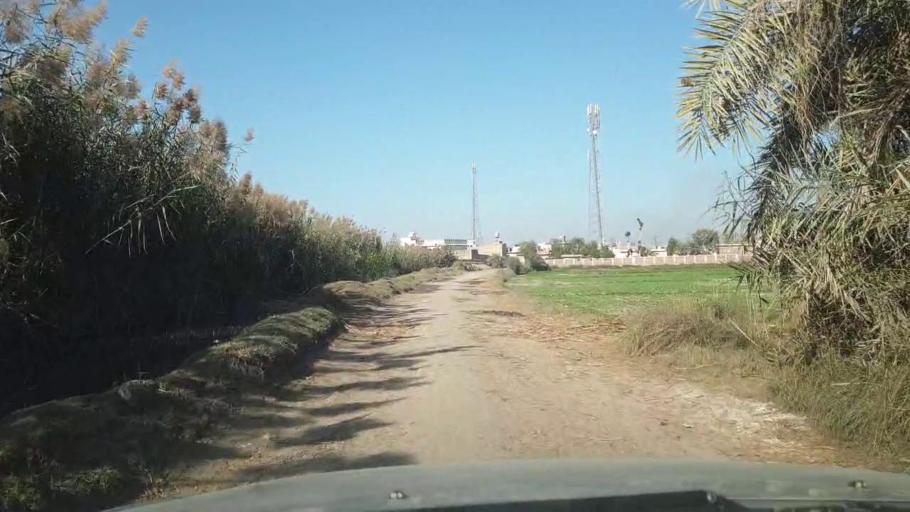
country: PK
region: Sindh
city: Ghotki
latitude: 28.0596
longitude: 69.3378
